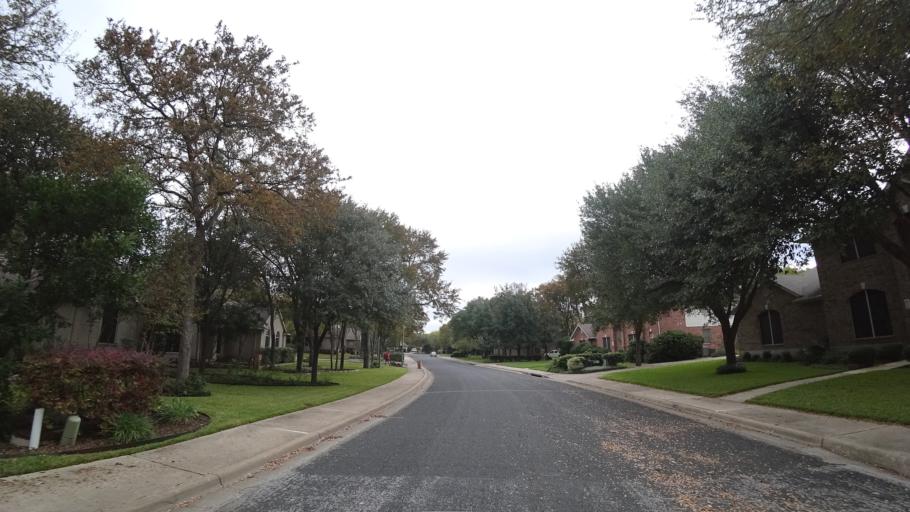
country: US
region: Texas
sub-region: Travis County
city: Shady Hollow
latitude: 30.1573
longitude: -97.8552
